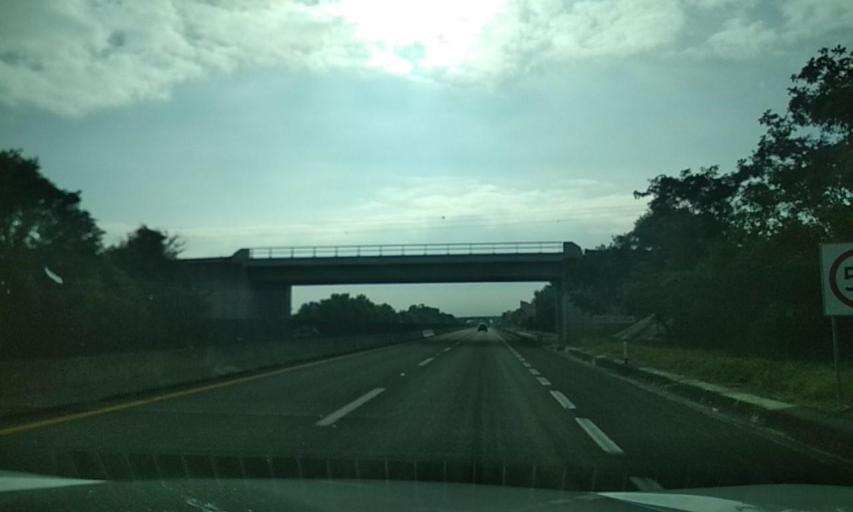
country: MX
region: Veracruz
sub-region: Emiliano Zapata
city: Plan del Rio
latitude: 19.3958
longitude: -96.6189
